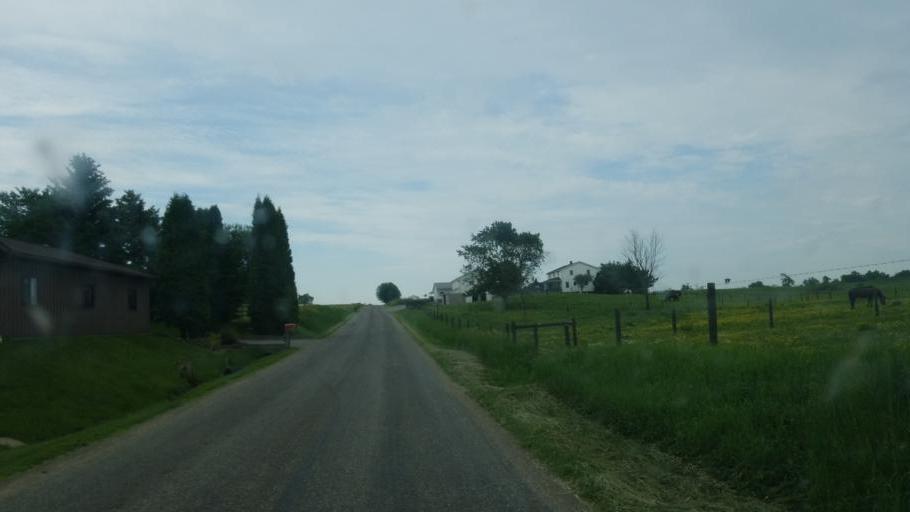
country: US
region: Ohio
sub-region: Wayne County
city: Apple Creek
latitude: 40.6892
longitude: -81.7652
